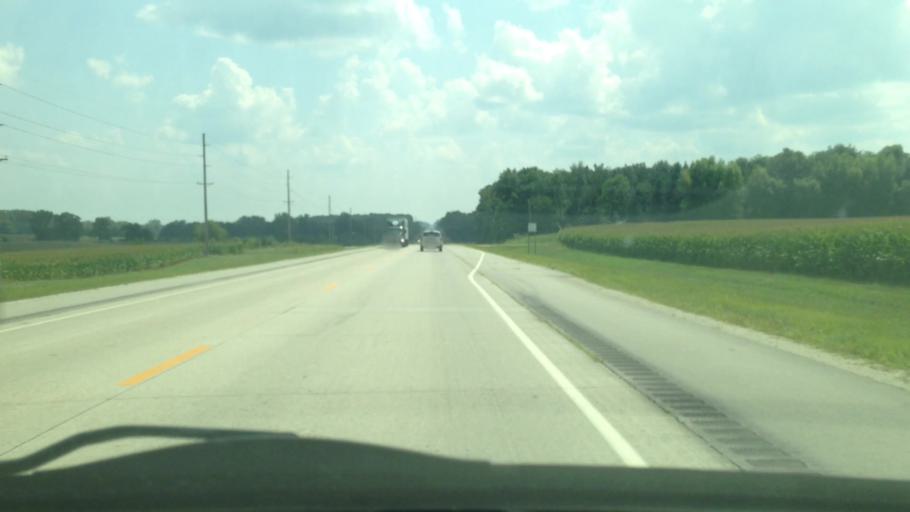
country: US
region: Minnesota
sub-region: Fillmore County
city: Spring Valley
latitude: 43.6328
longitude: -92.3897
